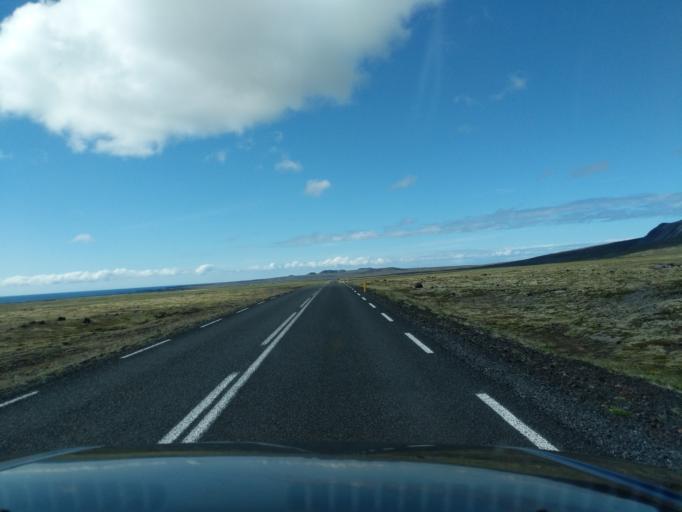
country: IS
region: West
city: Olafsvik
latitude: 64.7888
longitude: -23.9099
